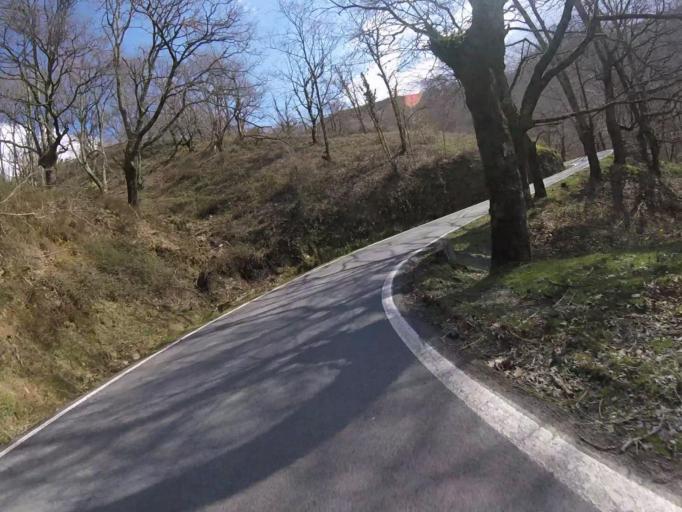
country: ES
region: Navarre
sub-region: Provincia de Navarra
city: Etxalar
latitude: 43.2520
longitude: -1.6148
